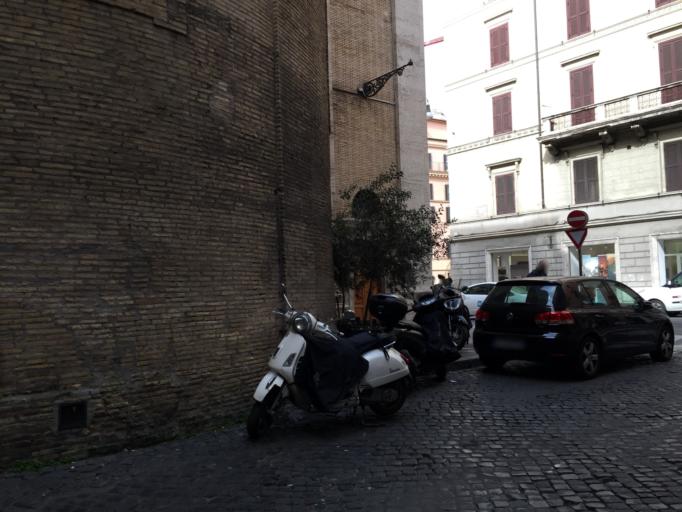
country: VA
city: Vatican City
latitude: 41.9017
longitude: 12.4821
